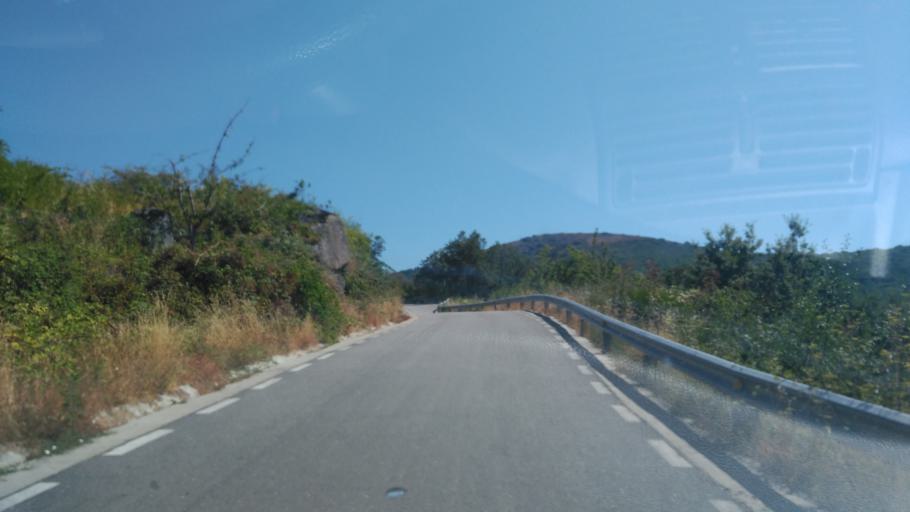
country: ES
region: Castille and Leon
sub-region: Provincia de Salamanca
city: San Martin del Castanar
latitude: 40.5243
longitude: -6.0599
